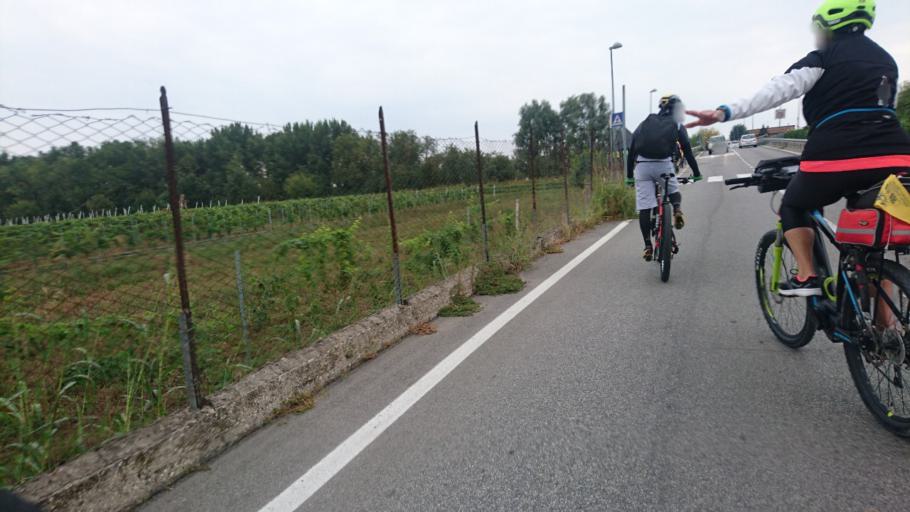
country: IT
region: Veneto
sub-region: Provincia di Verona
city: Verona
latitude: 45.4292
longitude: 11.0217
